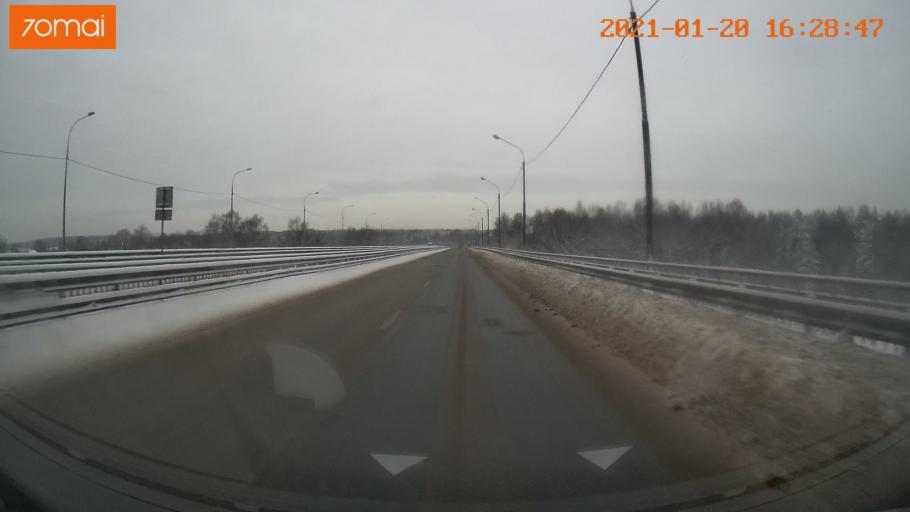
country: RU
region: Vladimir
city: Kameshkovo
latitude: 56.1964
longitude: 40.9094
